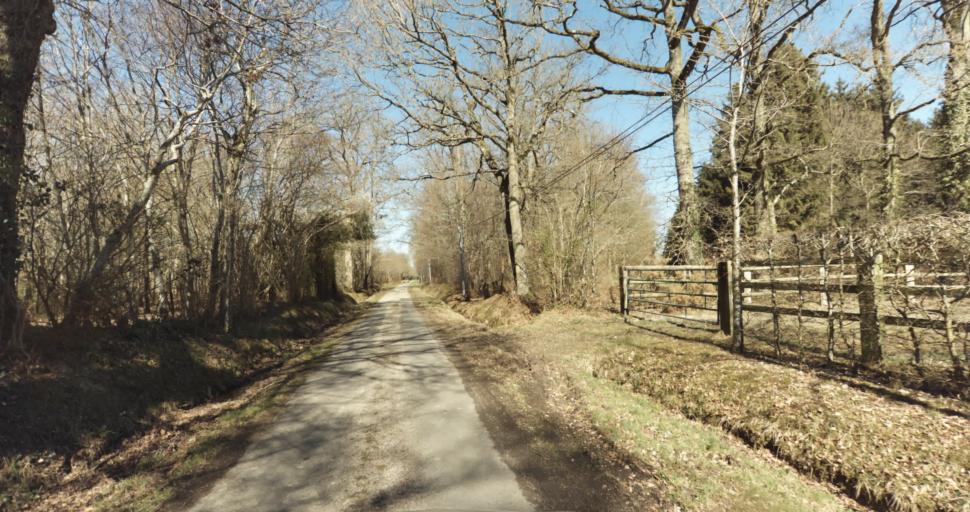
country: FR
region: Lower Normandy
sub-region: Departement du Calvados
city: Livarot
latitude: 48.9572
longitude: 0.0856
